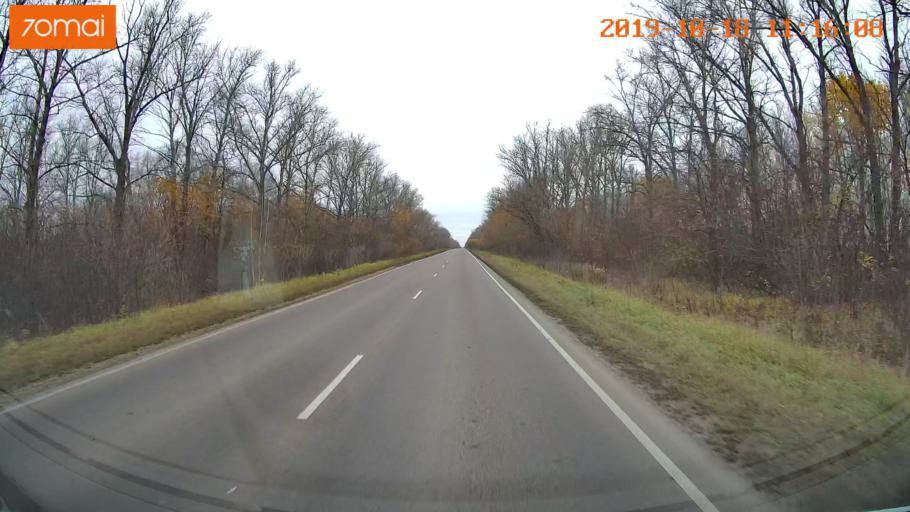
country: RU
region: Tula
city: Kimovsk
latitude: 54.0029
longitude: 38.5482
